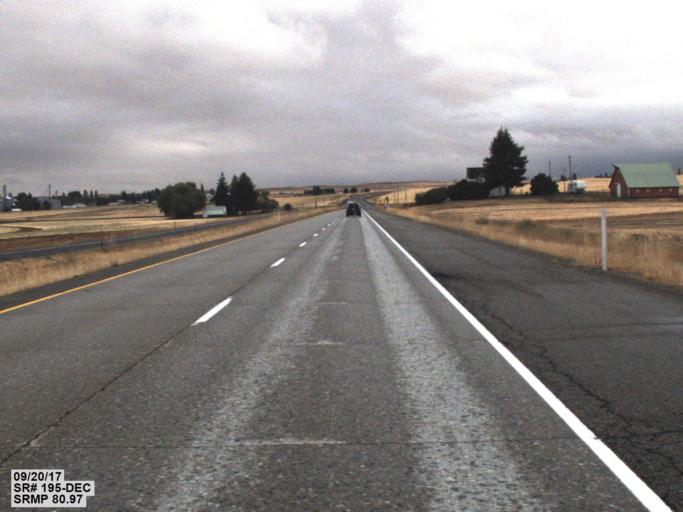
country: US
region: Washington
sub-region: Spokane County
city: Cheney
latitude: 47.4468
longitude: -117.3851
